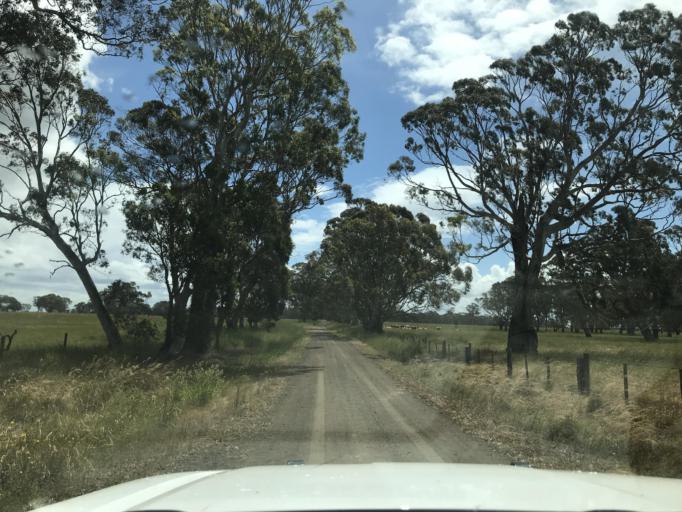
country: AU
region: South Australia
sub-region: Wattle Range
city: Penola
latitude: -37.1258
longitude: 141.3053
